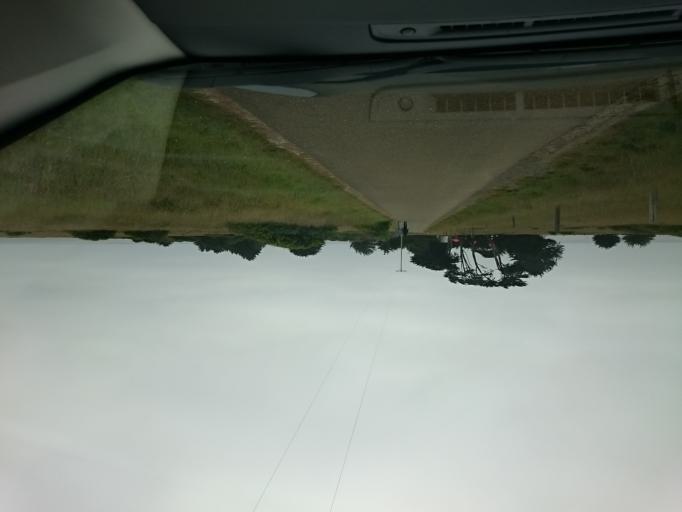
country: US
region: California
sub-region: Mendocino County
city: Fort Bragg
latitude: 39.3495
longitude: -123.8204
